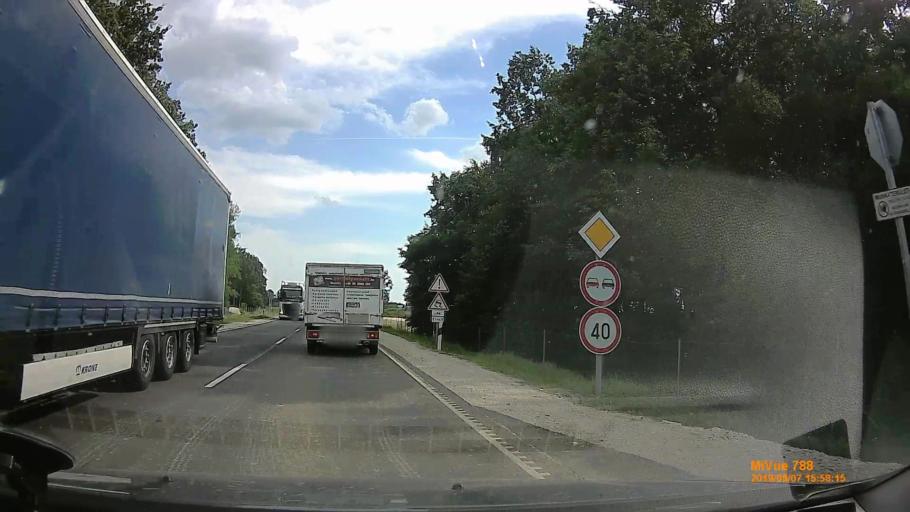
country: HU
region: Vas
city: Kormend
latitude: 47.0291
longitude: 16.6126
